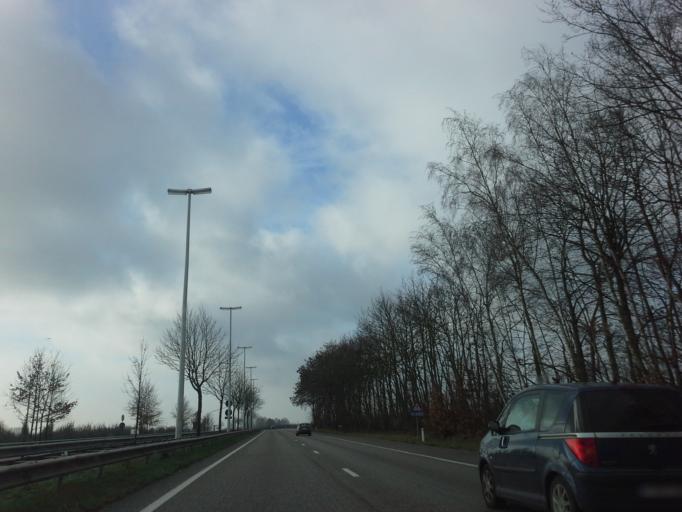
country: BE
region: Flanders
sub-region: Provincie Limburg
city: Nieuwerkerken
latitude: 50.8529
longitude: 5.2441
